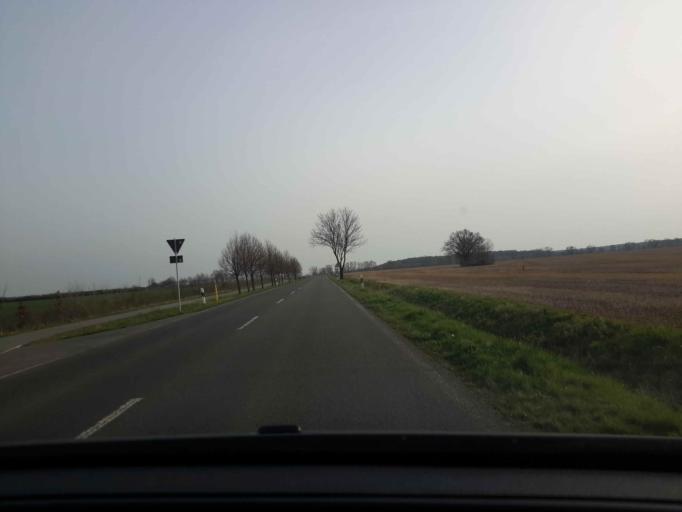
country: DE
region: Saxony
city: Rackwitz
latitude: 51.4320
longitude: 12.3551
